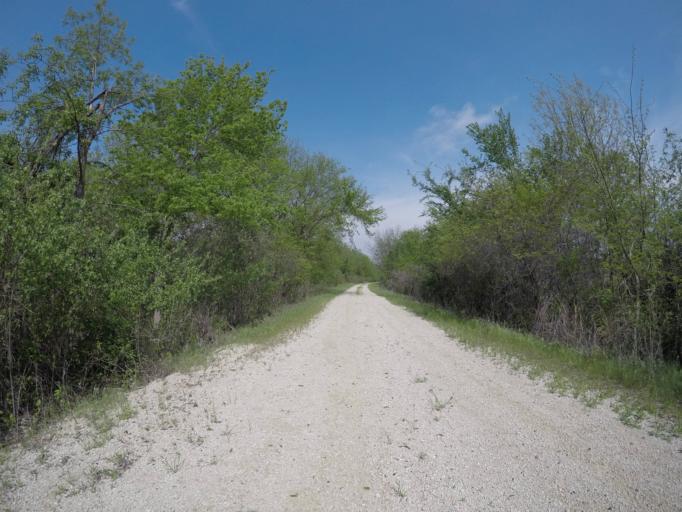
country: US
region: Nebraska
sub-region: Gage County
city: Wymore
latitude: 40.1038
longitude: -96.6139
